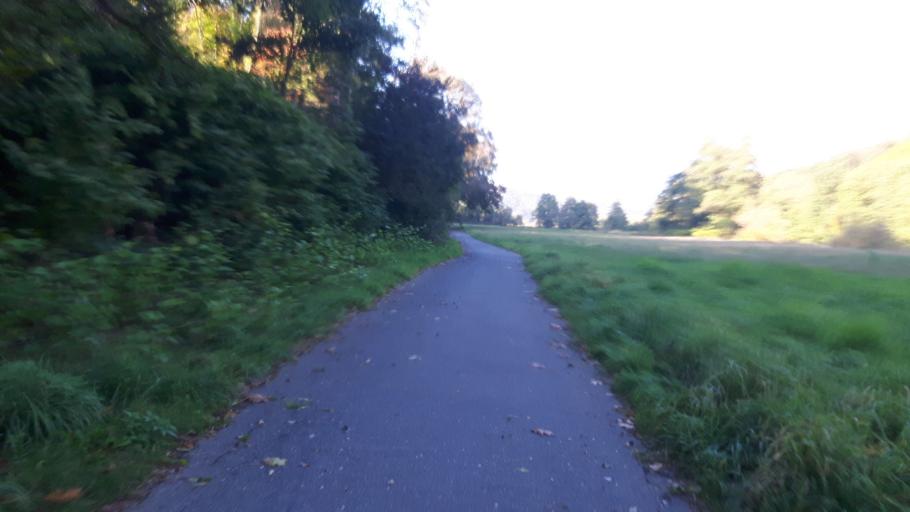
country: DE
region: Rheinland-Pfalz
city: Werkhausen
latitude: 50.7826
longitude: 7.5163
